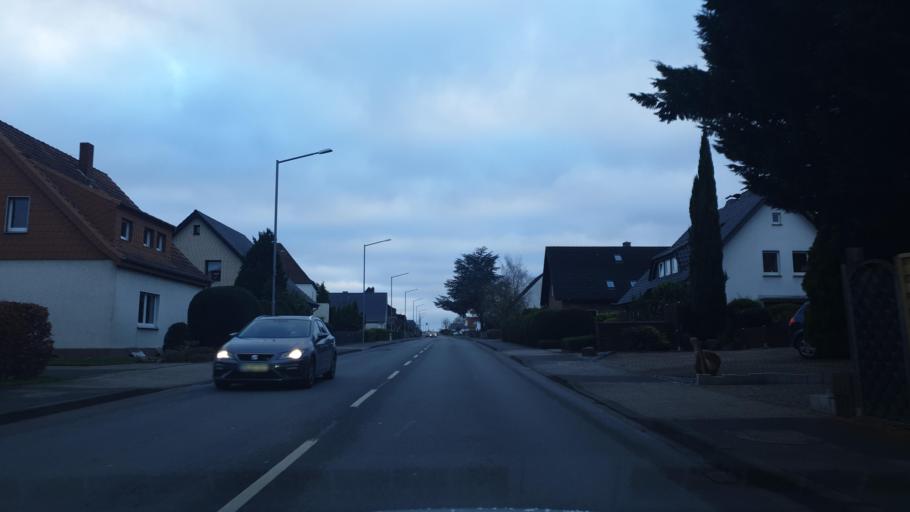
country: DE
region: North Rhine-Westphalia
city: Loehne
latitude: 52.1814
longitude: 8.6890
